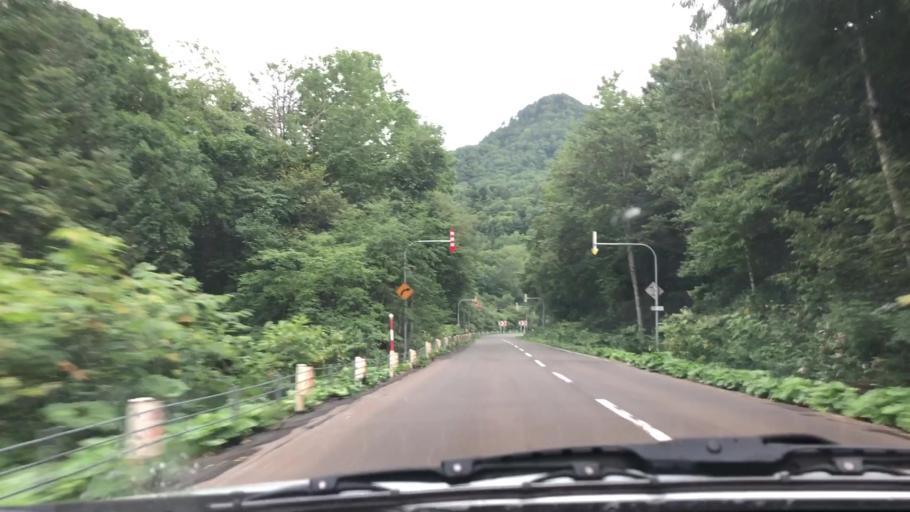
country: JP
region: Hokkaido
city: Shimo-furano
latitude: 42.9172
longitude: 142.3739
